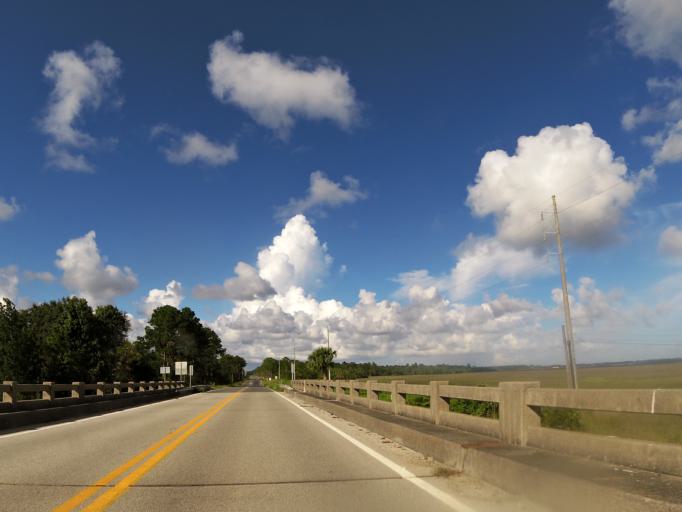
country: US
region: Georgia
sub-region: Glynn County
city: Brunswick
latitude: 31.1144
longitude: -81.6136
